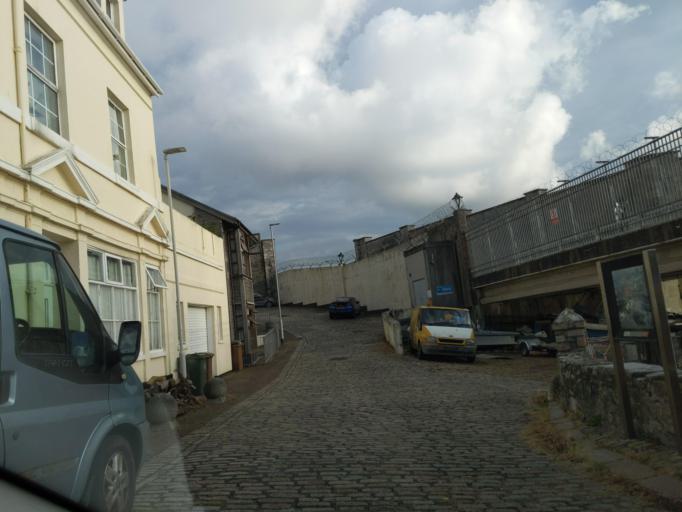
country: GB
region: England
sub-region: Cornwall
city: Millbrook
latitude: 50.3718
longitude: -4.1837
